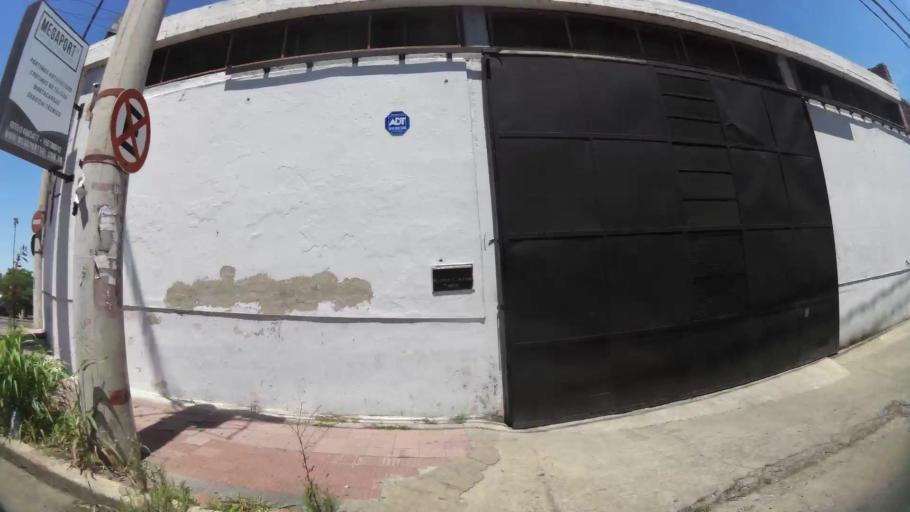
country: AR
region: Cordoba
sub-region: Departamento de Capital
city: Cordoba
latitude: -31.3963
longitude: -64.2029
